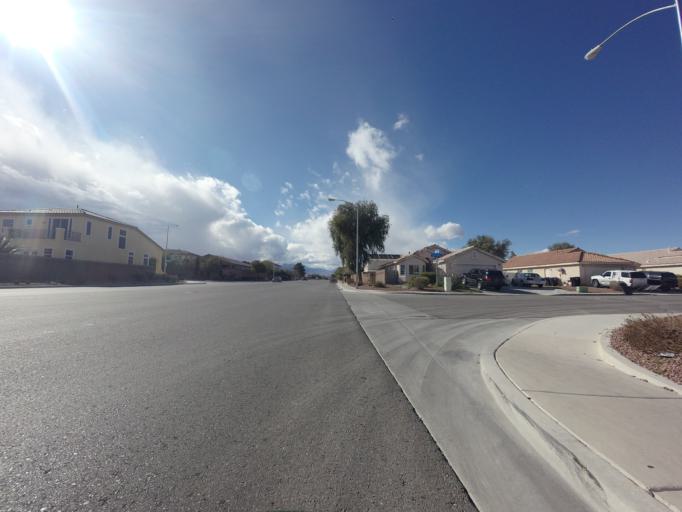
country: US
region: Nevada
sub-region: Clark County
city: North Las Vegas
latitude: 36.2544
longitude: -115.1230
